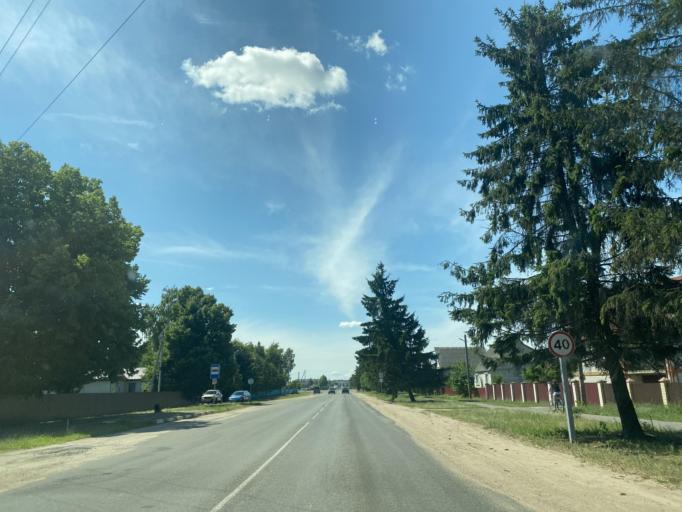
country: BY
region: Brest
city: Ivanava
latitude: 52.1603
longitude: 25.5460
